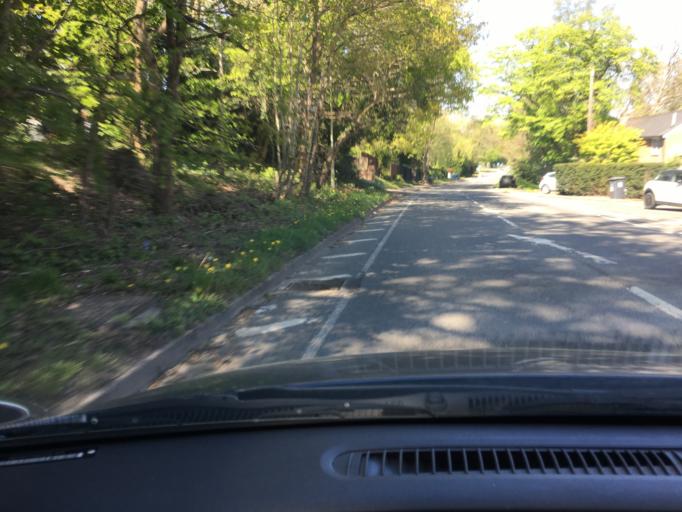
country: GB
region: England
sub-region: Hampshire
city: Yateley
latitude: 51.3341
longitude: -0.8210
